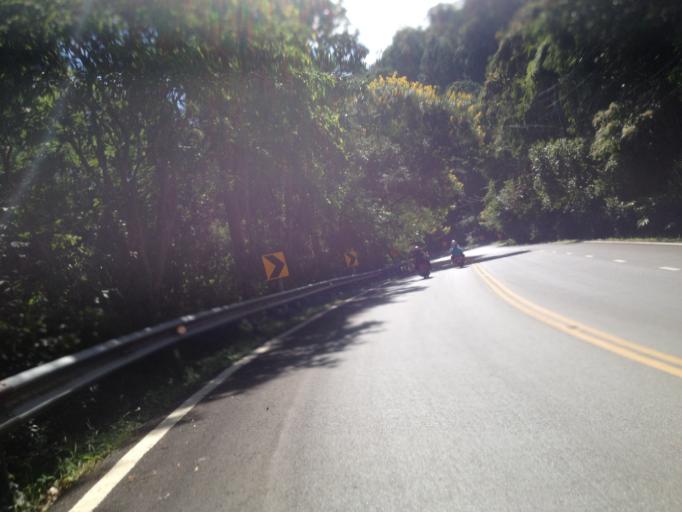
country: TH
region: Chiang Mai
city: Chiang Mai
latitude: 18.7964
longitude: 98.9230
